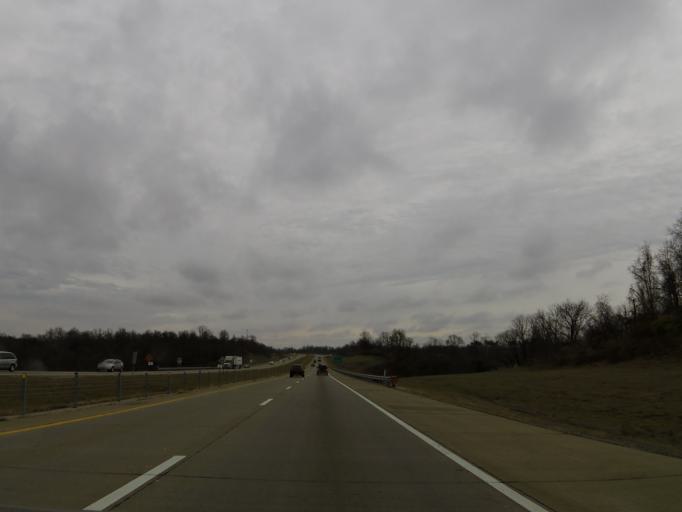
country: US
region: Indiana
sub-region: Dearborn County
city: Lawrenceburg
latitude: 39.0905
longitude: -84.8018
